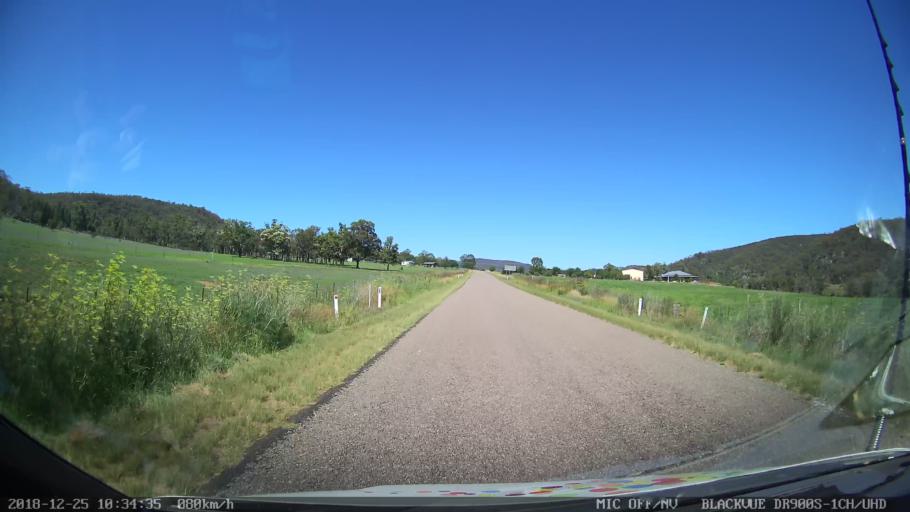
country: AU
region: New South Wales
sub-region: Upper Hunter Shire
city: Merriwa
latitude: -32.3929
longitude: 150.4062
